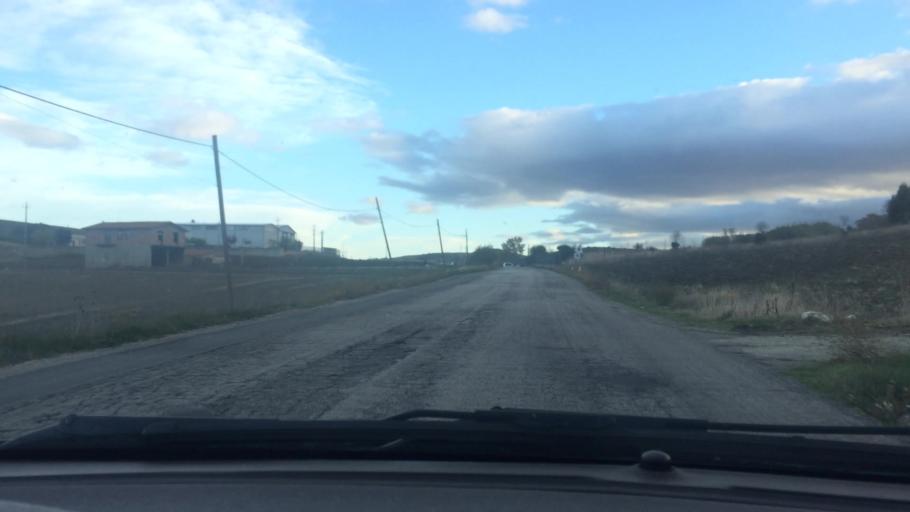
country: IT
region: Basilicate
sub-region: Provincia di Potenza
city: Tolve
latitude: 40.7090
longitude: 16.0179
